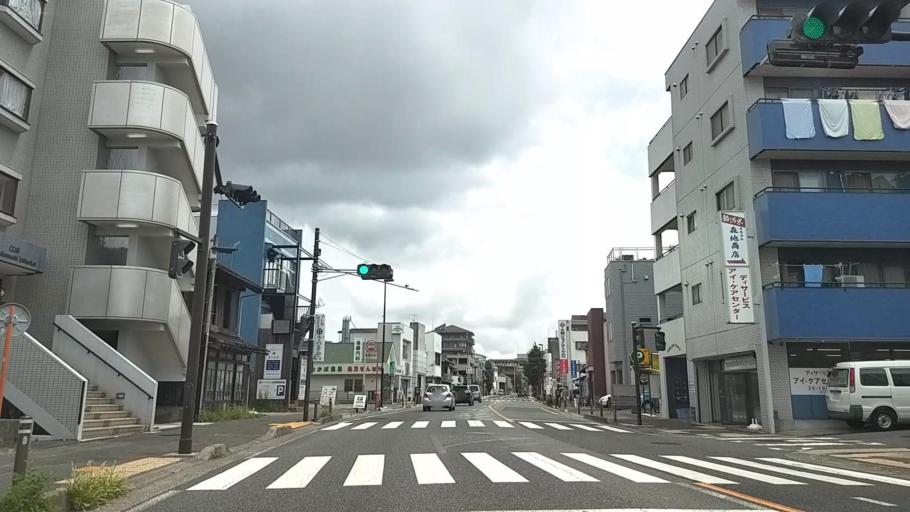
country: JP
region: Kanagawa
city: Fujisawa
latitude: 35.3478
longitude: 139.4821
